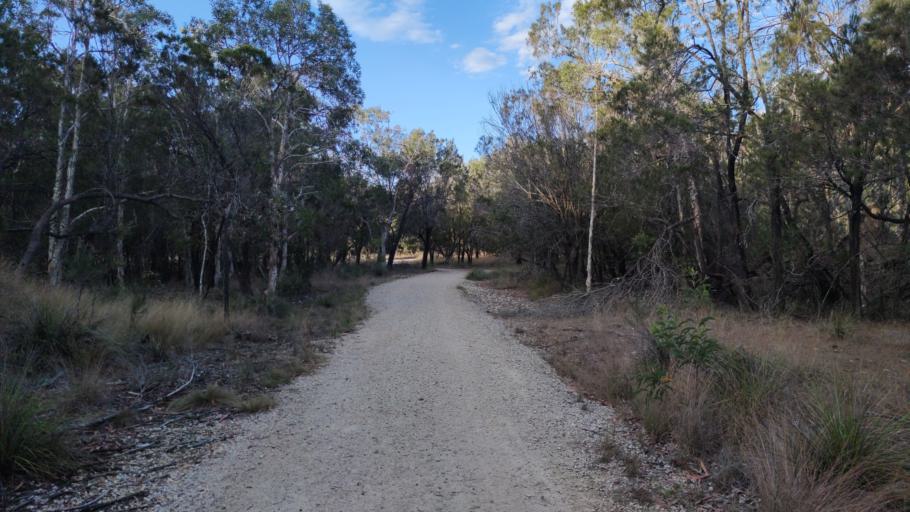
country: AU
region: Queensland
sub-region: Redland
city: Cleveland
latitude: -27.5503
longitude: 153.2435
